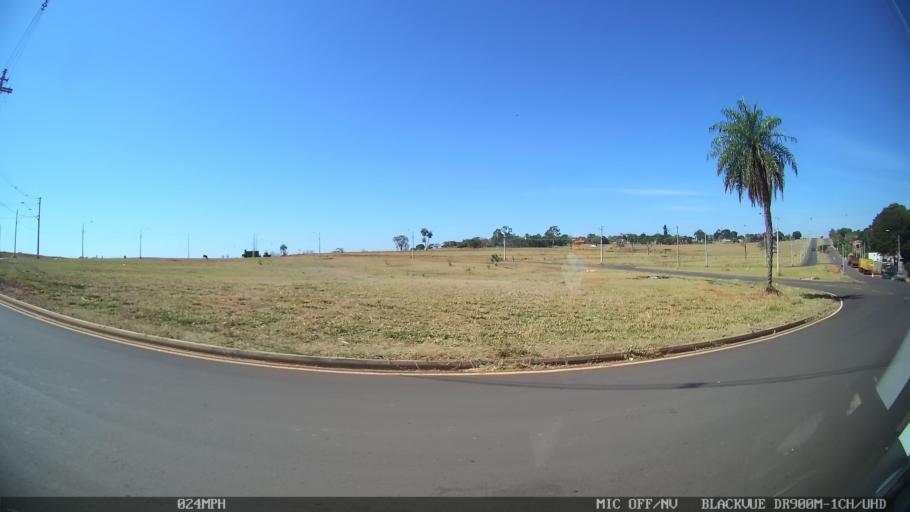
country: BR
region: Sao Paulo
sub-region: Sao Jose Do Rio Preto
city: Sao Jose do Rio Preto
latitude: -20.7273
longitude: -49.4391
